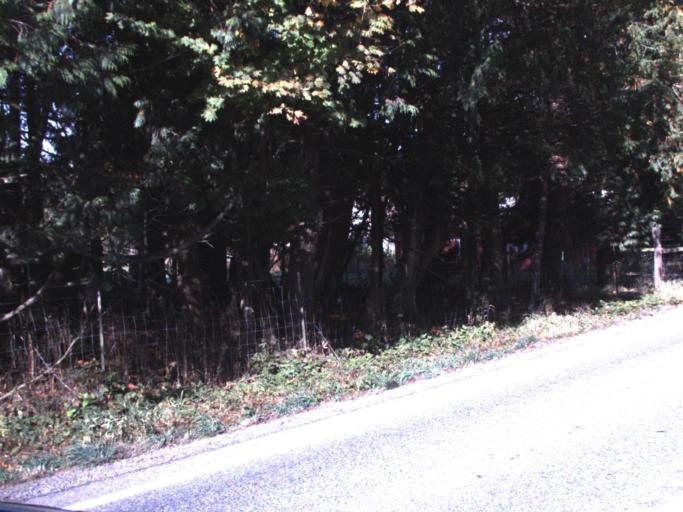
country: US
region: Washington
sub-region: Skagit County
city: Sedro-Woolley
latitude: 48.5641
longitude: -122.2246
